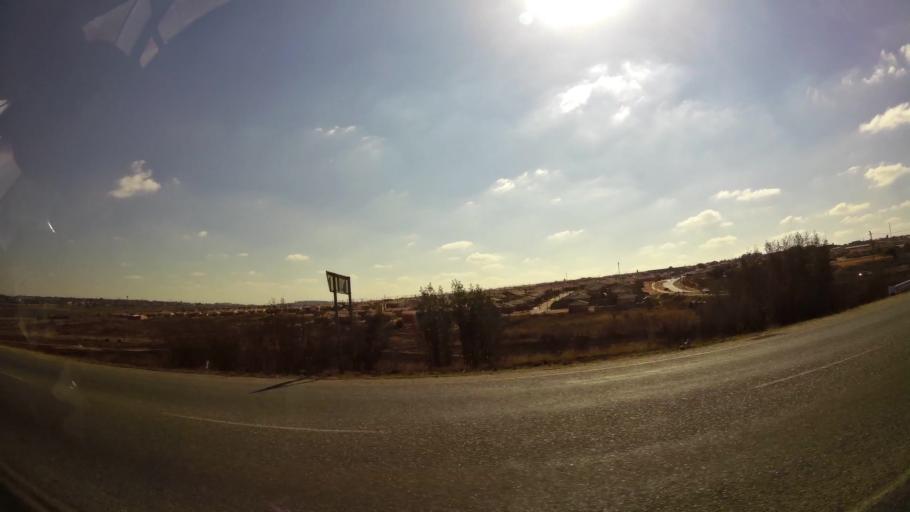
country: ZA
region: Gauteng
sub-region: West Rand District Municipality
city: Randfontein
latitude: -26.1743
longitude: 27.7774
